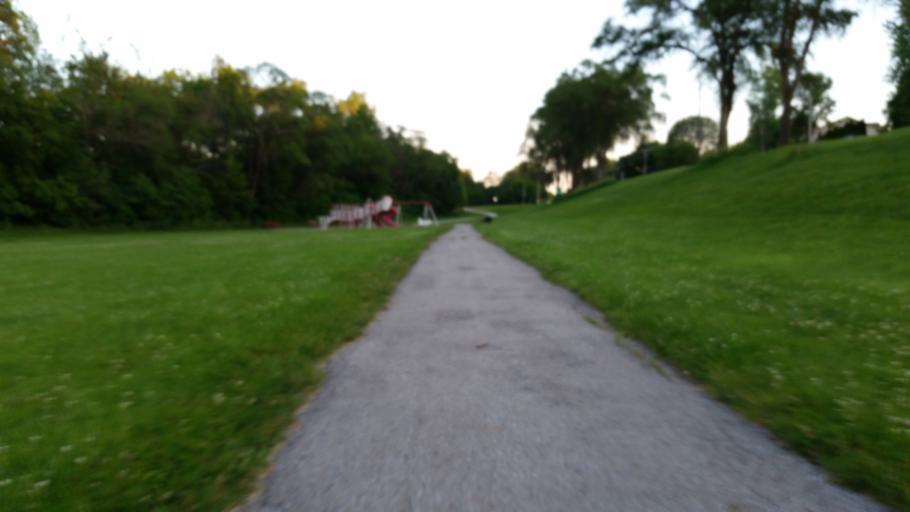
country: US
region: Nebraska
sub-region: Sarpy County
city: Offutt Air Force Base
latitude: 41.1145
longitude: -95.9470
